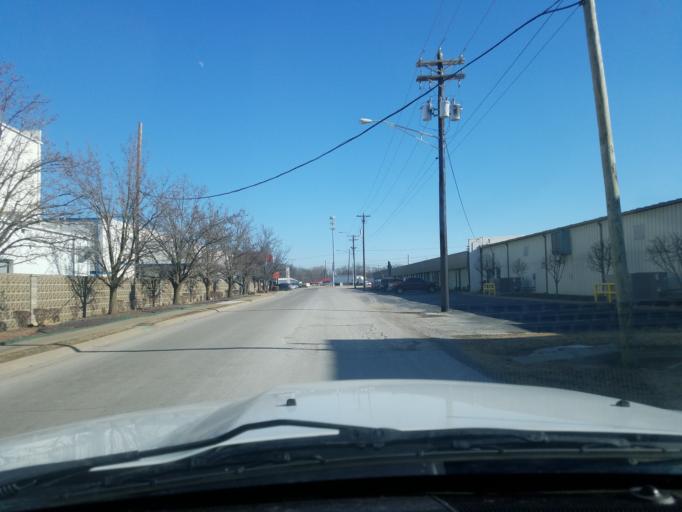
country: US
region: Kentucky
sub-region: Henderson County
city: Henderson
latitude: 37.8046
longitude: -87.6397
